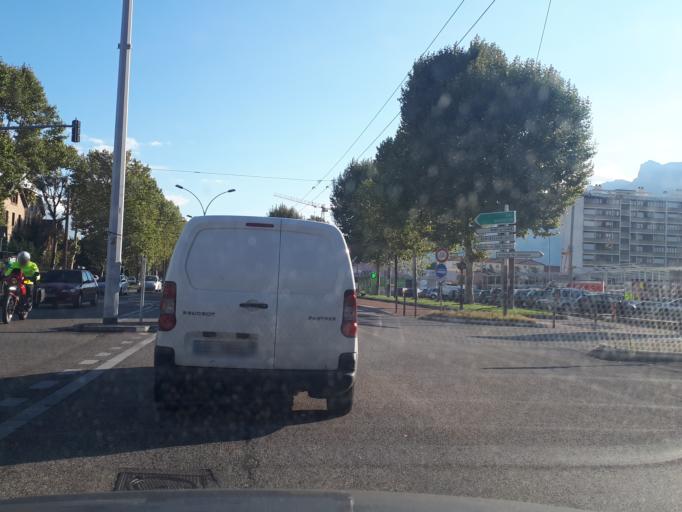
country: FR
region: Rhone-Alpes
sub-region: Departement de l'Isere
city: Grenoble
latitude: 45.1521
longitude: 5.7069
